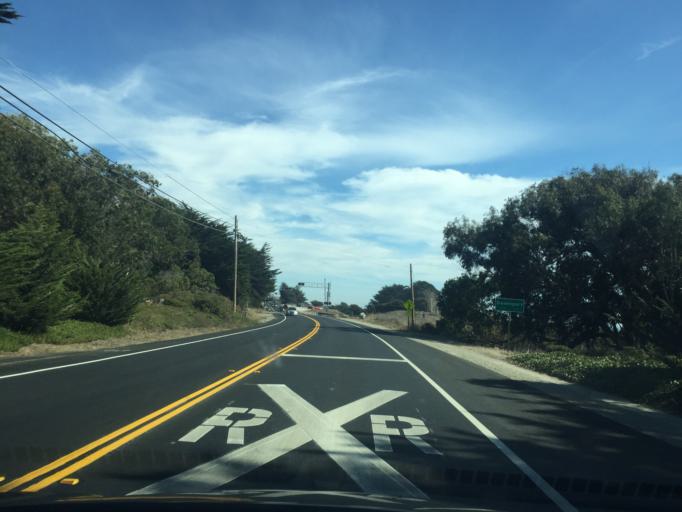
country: US
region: California
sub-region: Santa Cruz County
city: Bonny Doon
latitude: 37.0145
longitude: -122.2009
